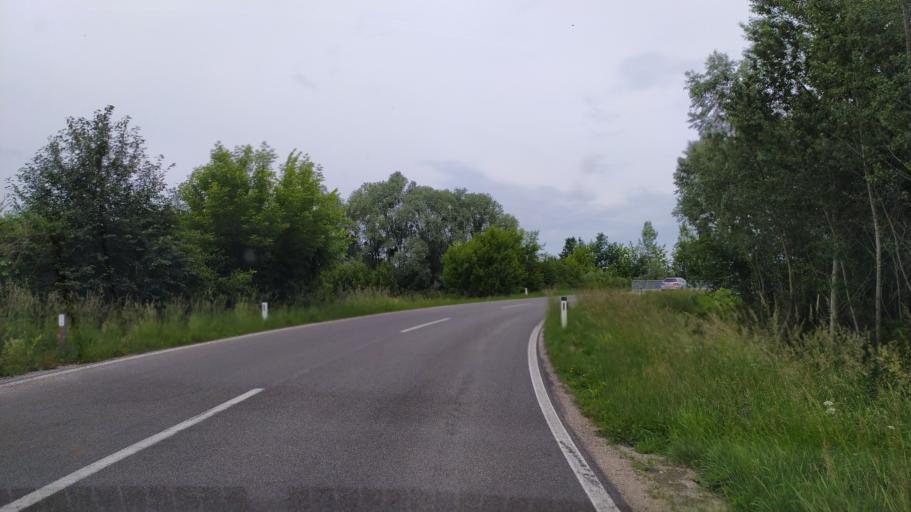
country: AT
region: Lower Austria
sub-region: Politischer Bezirk Amstetten
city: Strengberg
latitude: 48.1752
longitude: 14.7030
